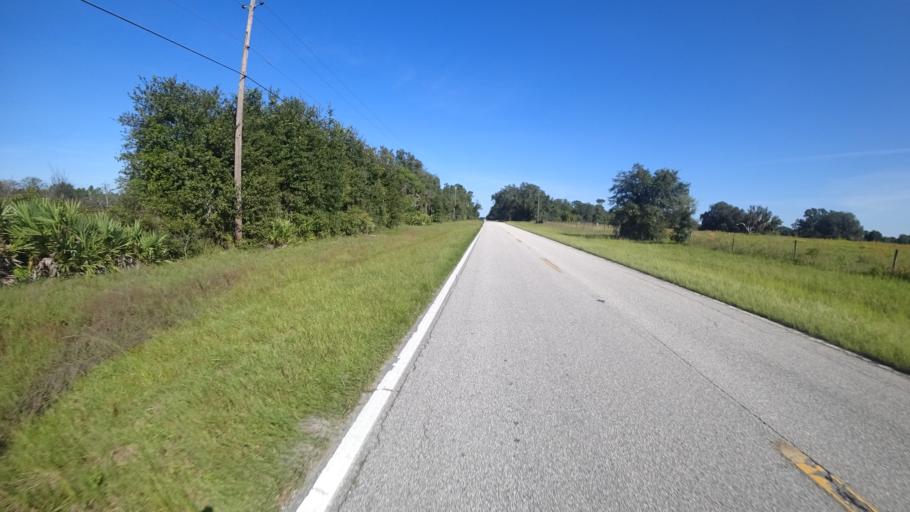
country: US
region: Florida
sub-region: Hillsborough County
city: Wimauma
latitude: 27.6523
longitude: -82.2943
